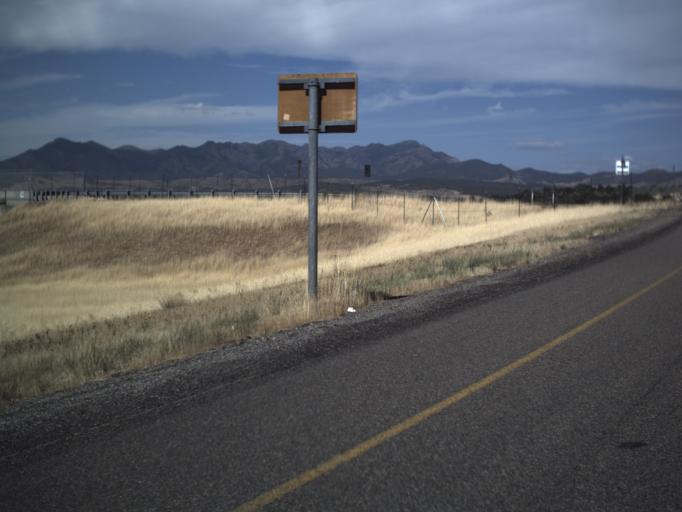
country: US
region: Utah
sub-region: Millard County
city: Fillmore
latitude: 39.0813
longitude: -112.2761
